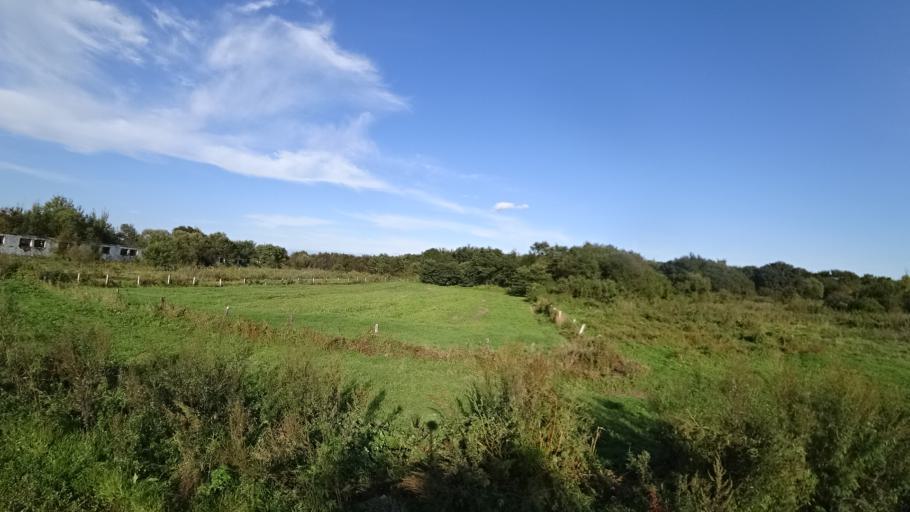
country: RU
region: Amur
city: Arkhara
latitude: 49.3483
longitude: 130.1066
